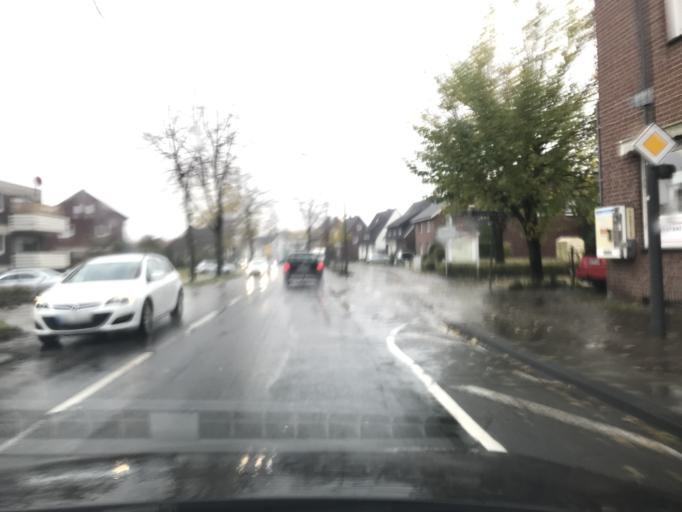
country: DE
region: North Rhine-Westphalia
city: Oelde
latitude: 51.8152
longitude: 8.1379
